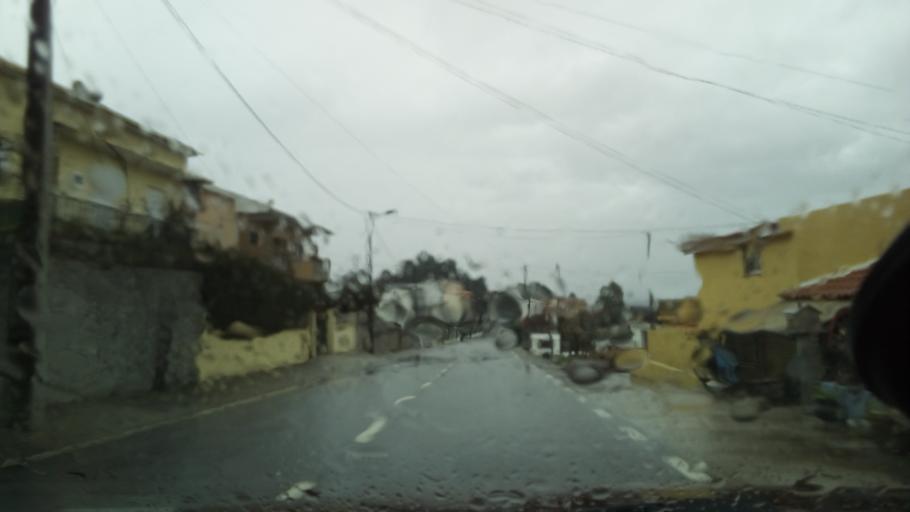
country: PT
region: Guarda
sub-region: Fornos de Algodres
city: Fornos de Algodres
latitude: 40.5249
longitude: -7.5797
